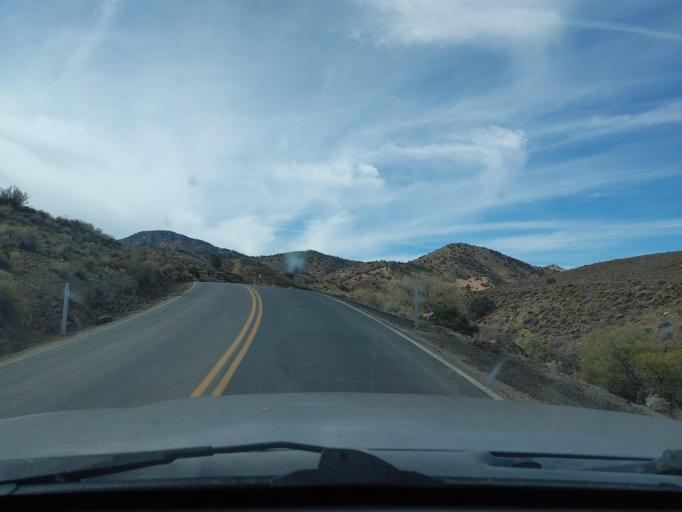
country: US
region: Nevada
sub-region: Lyon County
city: Dayton
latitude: 39.3057
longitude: -119.5642
